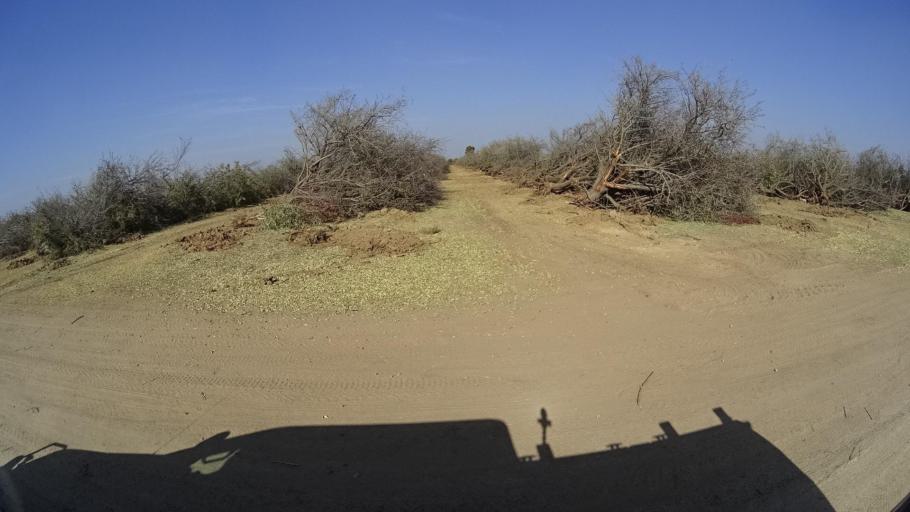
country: US
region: California
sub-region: Kern County
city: Shafter
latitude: 35.5444
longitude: -119.1357
